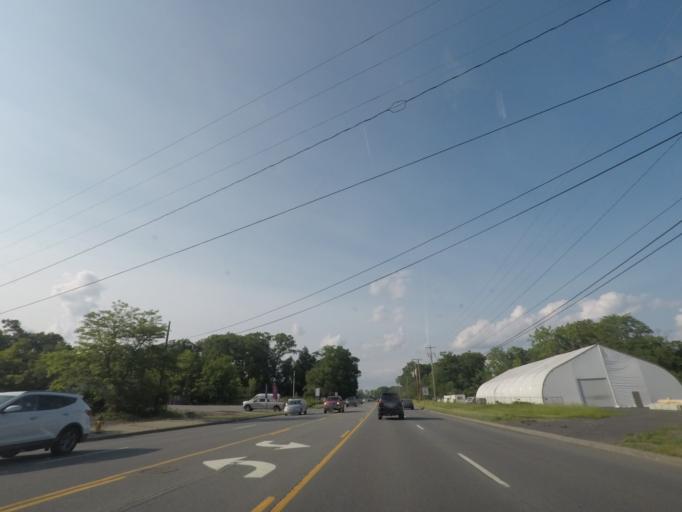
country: US
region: New York
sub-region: Orange County
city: Vails Gate
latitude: 41.4889
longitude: -74.0773
